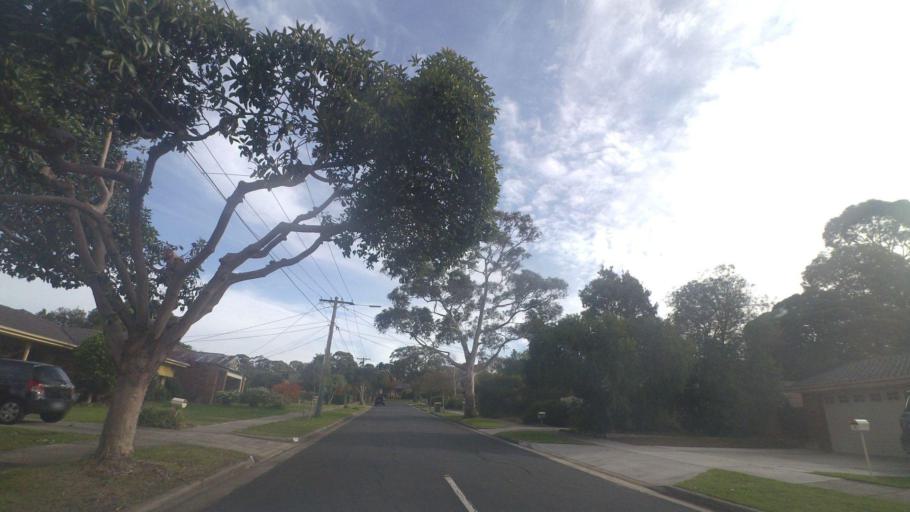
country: AU
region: Victoria
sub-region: Whitehorse
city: Vermont South
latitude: -37.8586
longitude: 145.1895
